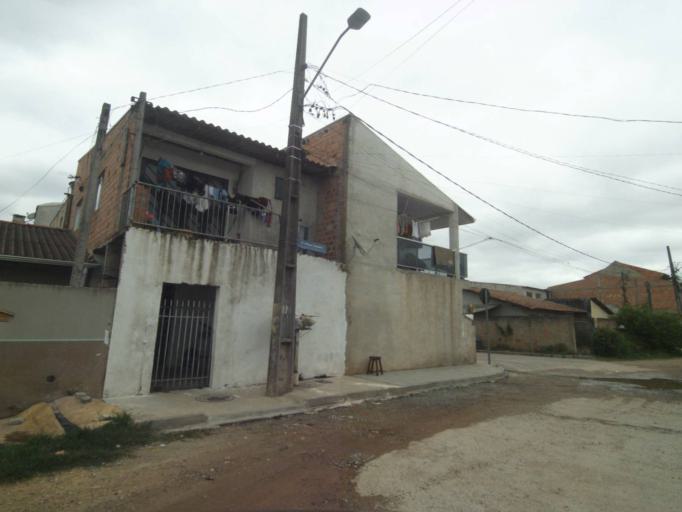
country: BR
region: Parana
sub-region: Pinhais
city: Pinhais
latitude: -25.4574
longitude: -49.1953
